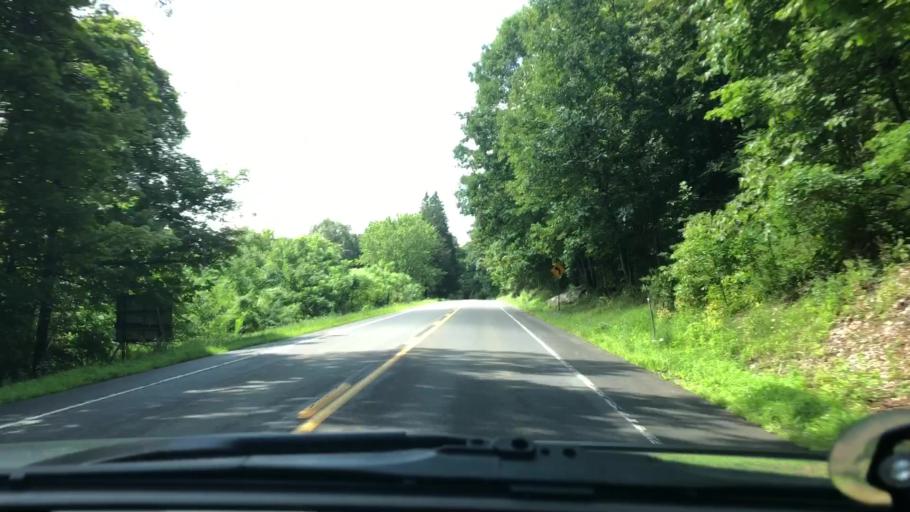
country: US
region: New York
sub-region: Greene County
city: Palenville
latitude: 42.2010
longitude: -73.9852
